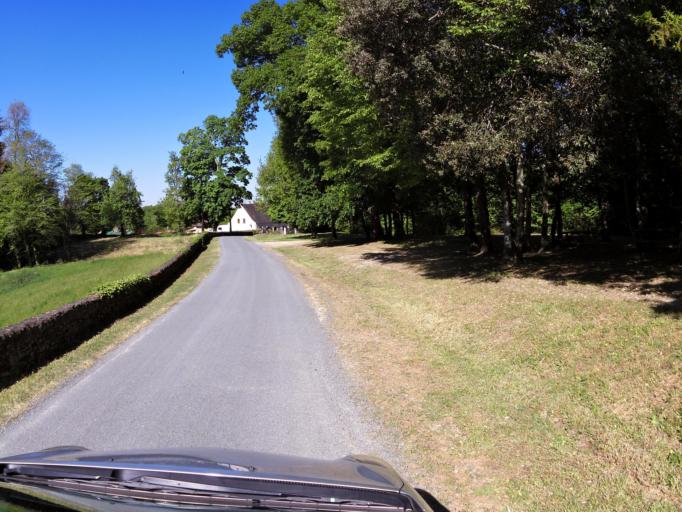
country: FR
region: Aquitaine
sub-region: Departement de la Dordogne
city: Eyvigues-et-Eybenes
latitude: 44.8423
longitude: 1.3465
